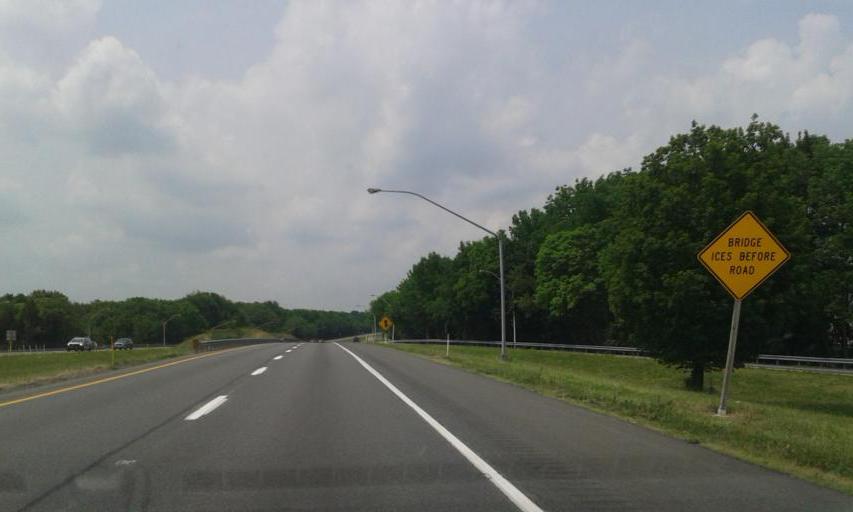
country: US
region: Pennsylvania
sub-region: Northampton County
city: Belfast
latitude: 40.7789
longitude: -75.2828
